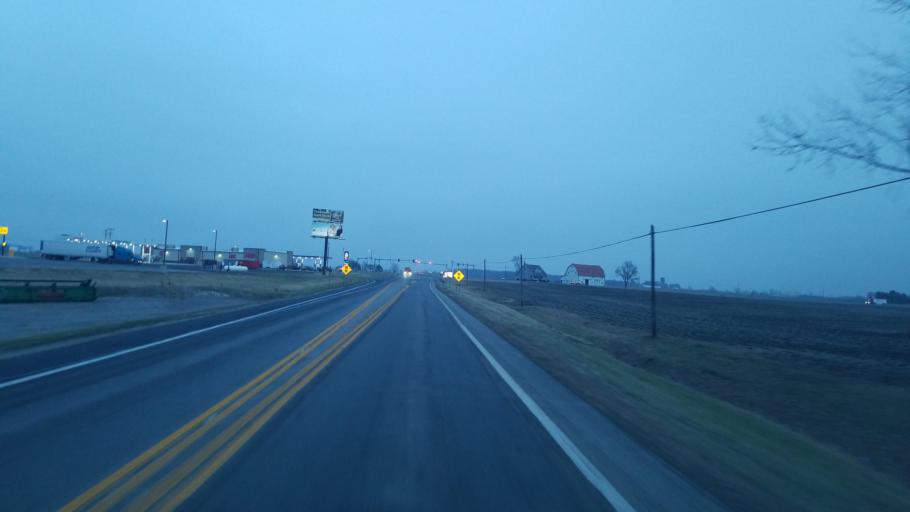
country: US
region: Ohio
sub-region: Mercer County
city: Rockford
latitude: 40.6529
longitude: -84.5845
